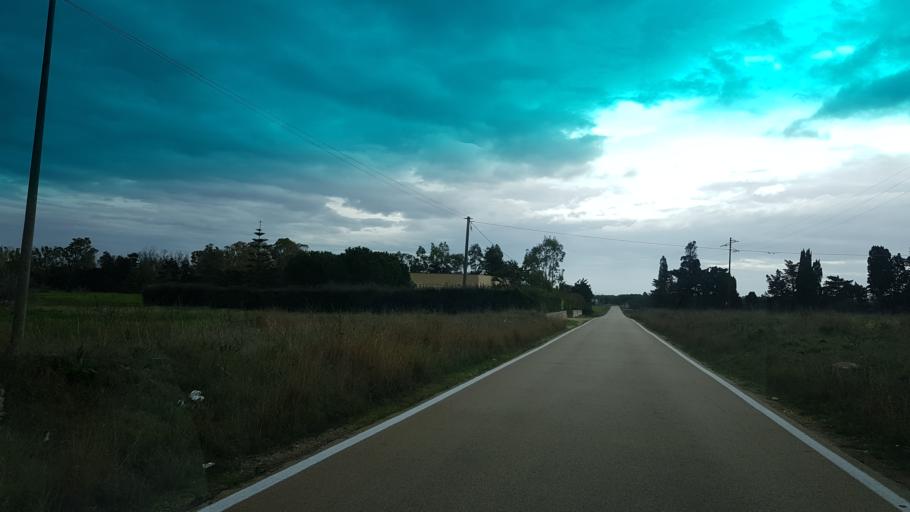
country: IT
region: Apulia
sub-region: Provincia di Brindisi
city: San Vito dei Normanni
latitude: 40.7136
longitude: 17.7653
